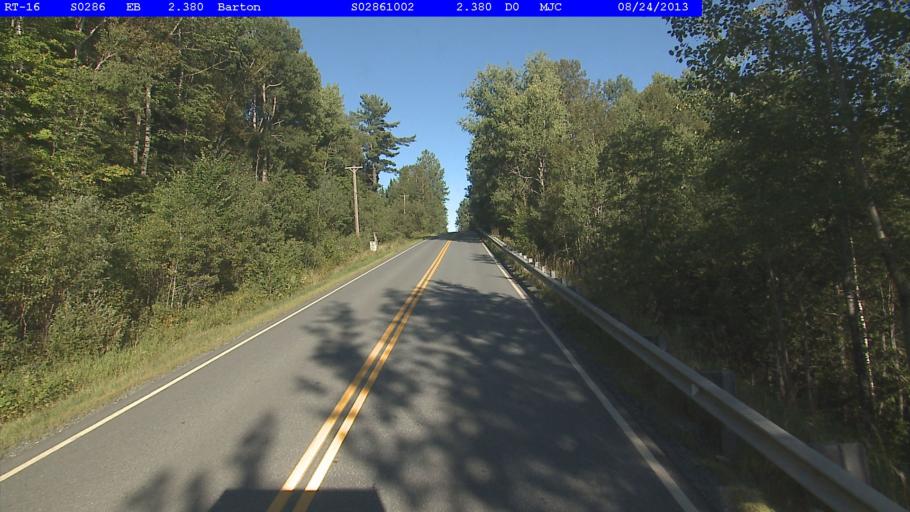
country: US
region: Vermont
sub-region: Orleans County
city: Newport
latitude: 44.7633
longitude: -72.1387
